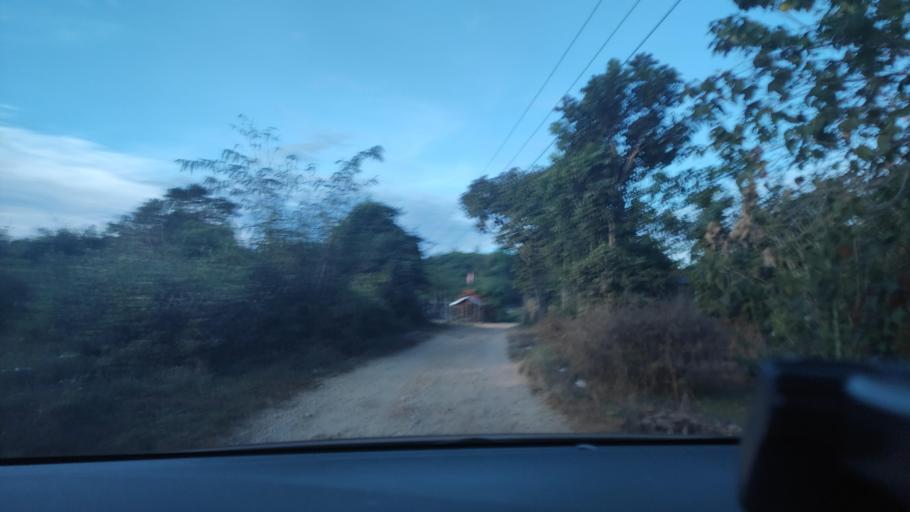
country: PH
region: Ilocos
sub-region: Province of Pangasinan
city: Balingasay
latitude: 16.3066
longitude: 119.8613
